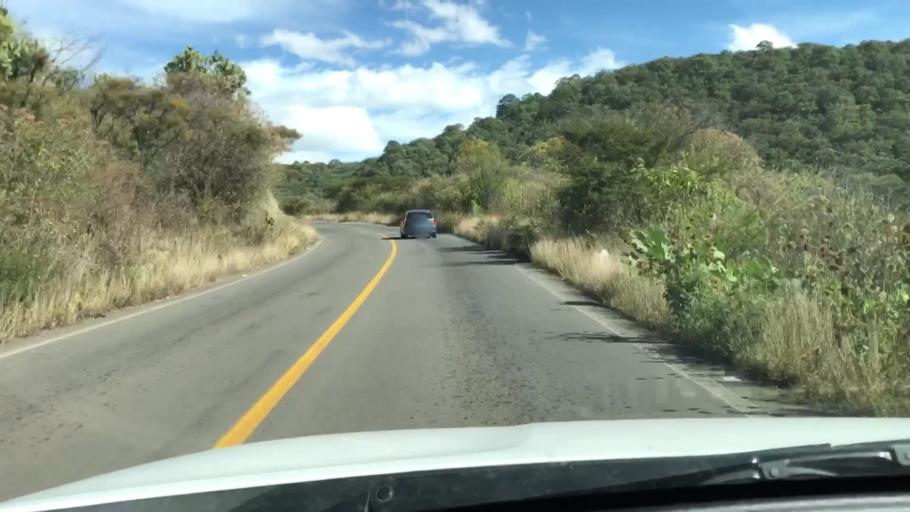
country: MX
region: Jalisco
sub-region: Zacoalco de Torres
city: Barranca de Otates (Barranca de Otatan)
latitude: 20.1924
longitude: -103.6975
